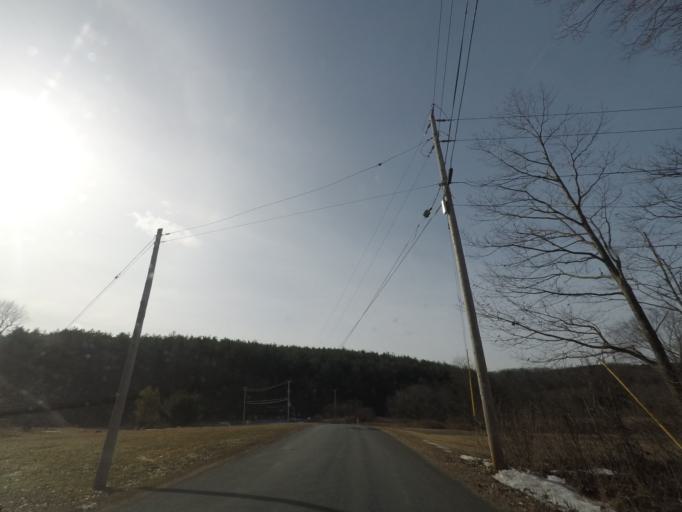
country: US
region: New York
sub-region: Rensselaer County
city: Nassau
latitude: 42.5100
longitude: -73.5629
